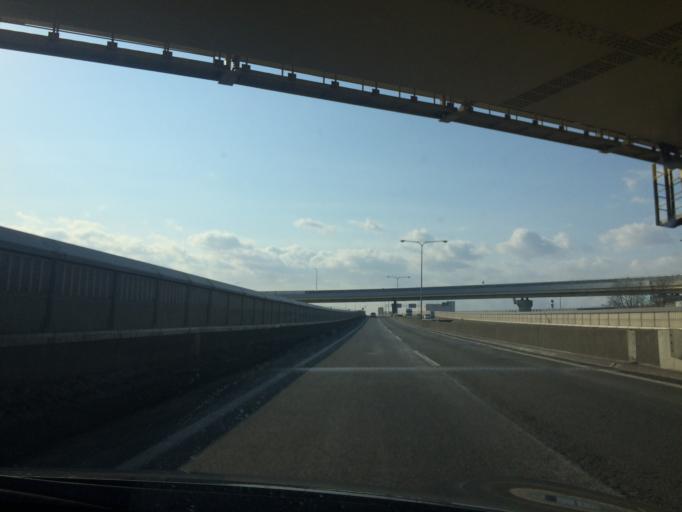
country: JP
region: Hokkaido
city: Sapporo
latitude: 43.0780
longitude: 141.4204
